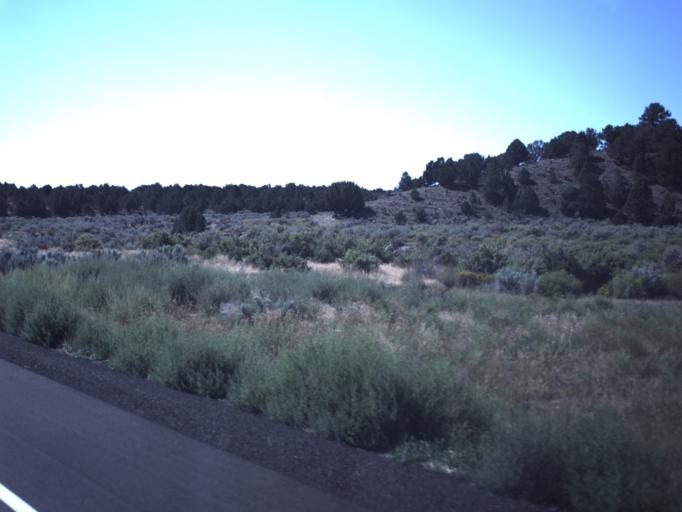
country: US
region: Utah
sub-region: Utah County
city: Eagle Mountain
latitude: 39.9898
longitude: -112.2668
